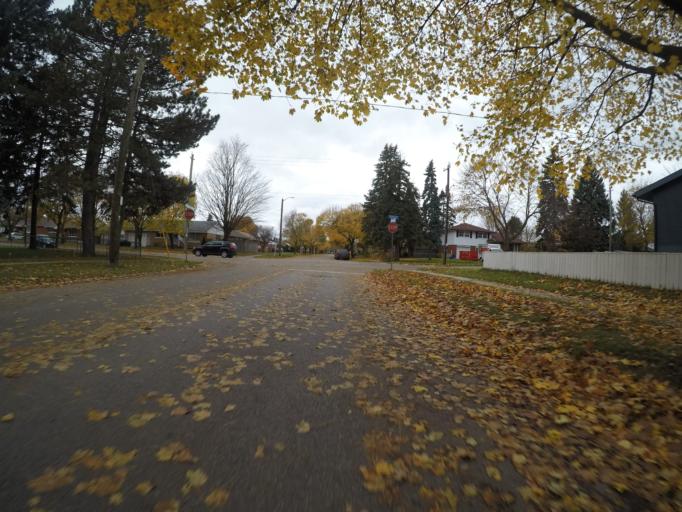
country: CA
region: Ontario
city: Kitchener
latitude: 43.4275
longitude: -80.4520
